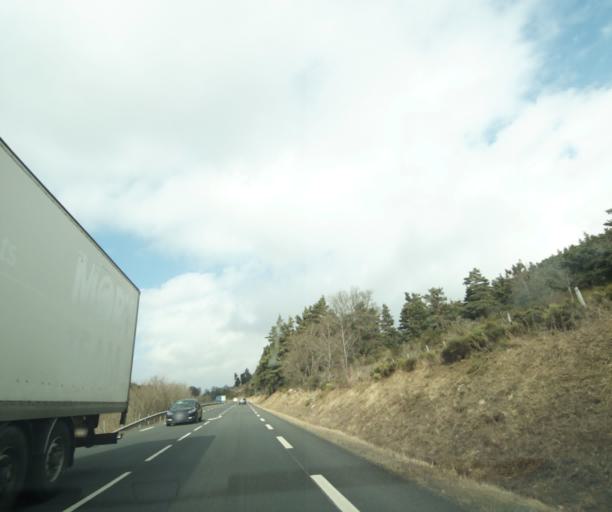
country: FR
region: Languedoc-Roussillon
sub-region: Departement de la Lozere
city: Mende
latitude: 44.6092
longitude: 3.6760
